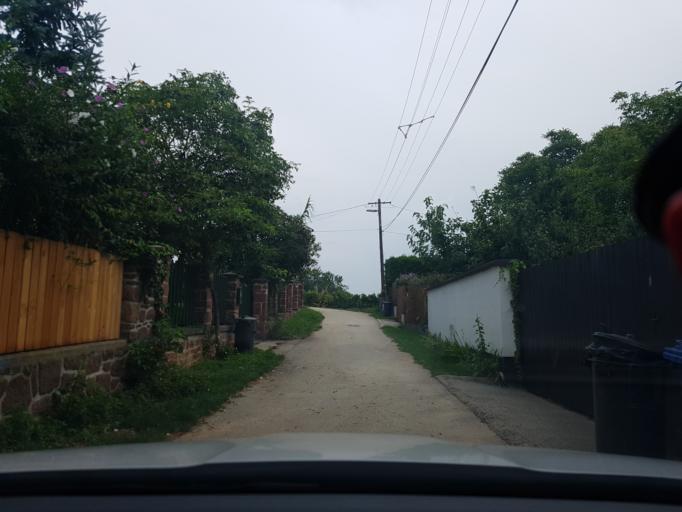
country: HU
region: Veszprem
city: Balatonalmadi
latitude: 46.9921
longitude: 17.9841
